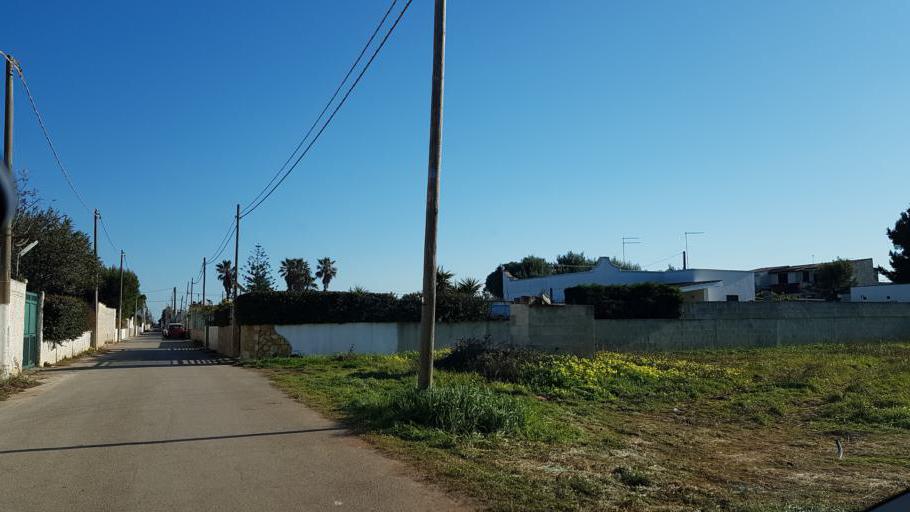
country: IT
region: Apulia
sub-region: Provincia di Brindisi
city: Materdomini
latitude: 40.6760
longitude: 17.9402
